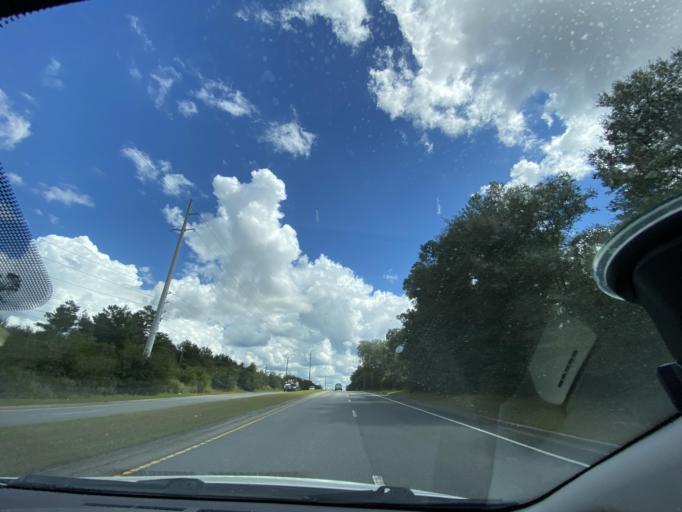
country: US
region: Florida
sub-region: Marion County
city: Belleview
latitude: 29.0259
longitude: -82.1926
